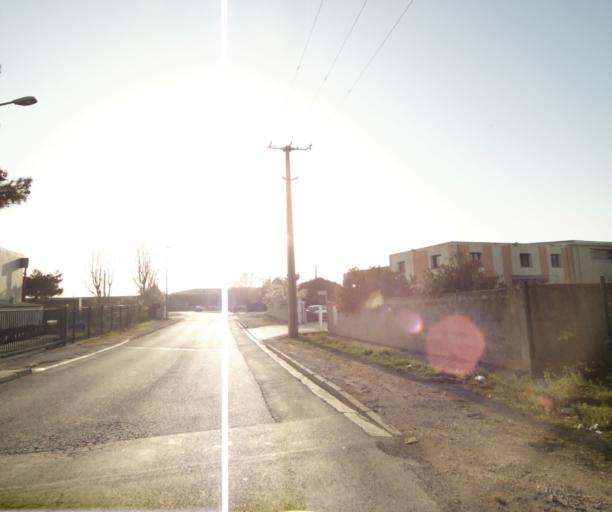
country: FR
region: Provence-Alpes-Cote d'Azur
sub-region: Departement des Bouches-du-Rhone
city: Saint-Victoret
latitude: 43.4277
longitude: 5.2476
